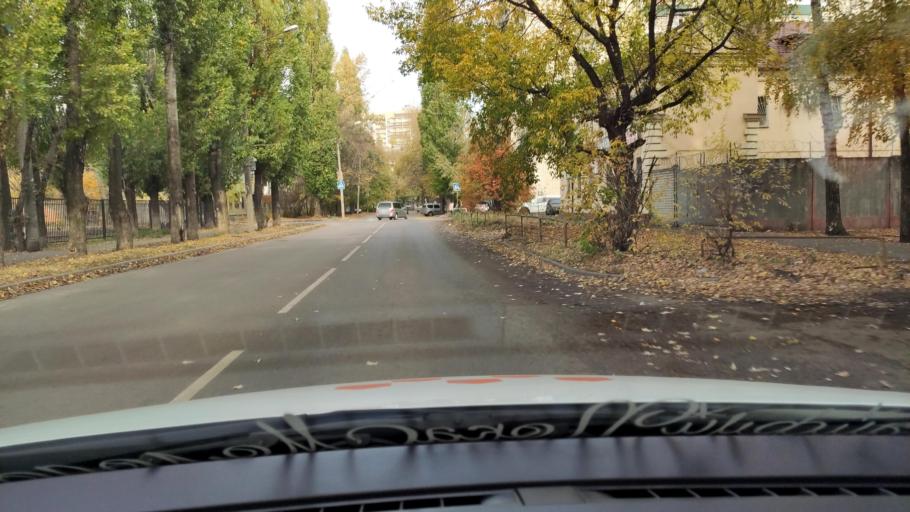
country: RU
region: Voronezj
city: Voronezh
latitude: 51.6819
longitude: 39.1958
